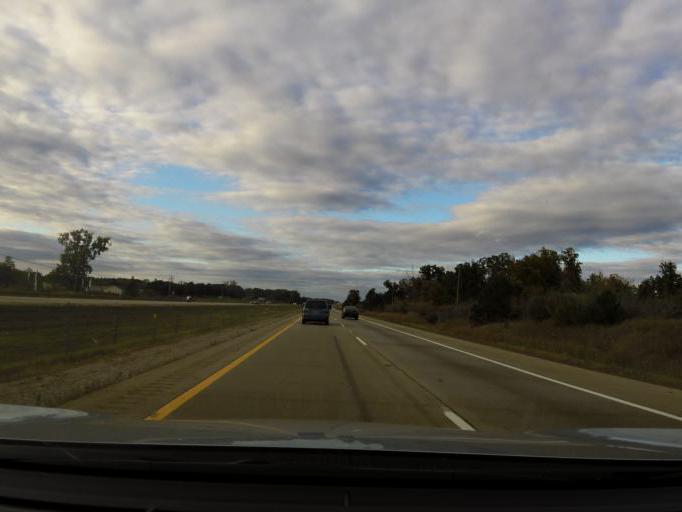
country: US
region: Michigan
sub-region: Genesee County
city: Fenton
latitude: 42.6938
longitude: -83.7609
